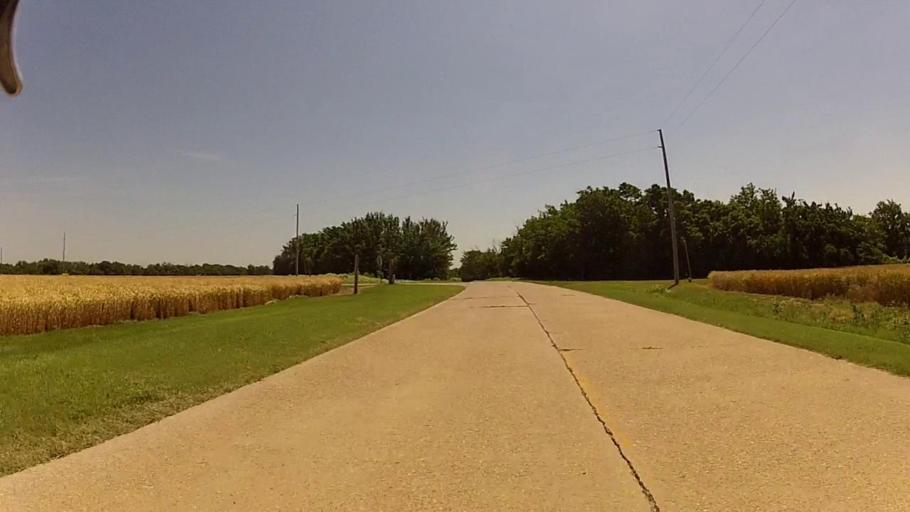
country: US
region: Kansas
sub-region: Sumner County
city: Caldwell
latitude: 37.0337
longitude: -97.4926
